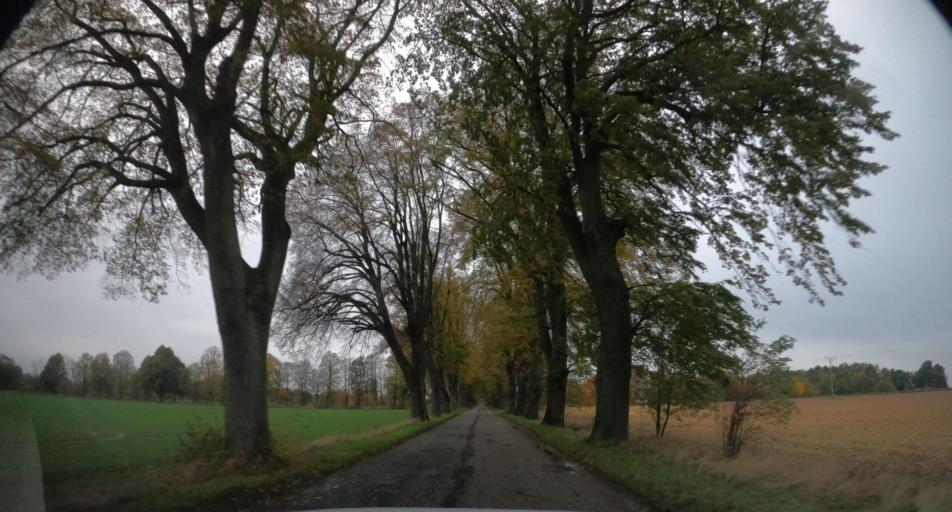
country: PL
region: West Pomeranian Voivodeship
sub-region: Powiat kamienski
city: Wolin
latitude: 53.9048
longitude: 14.6226
